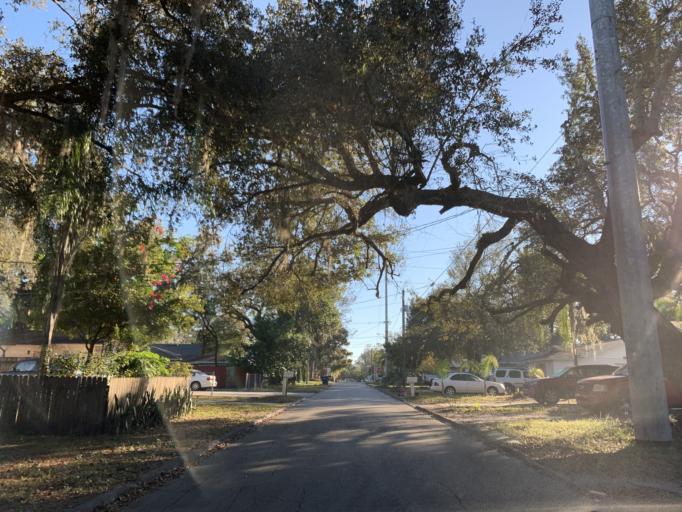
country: US
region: Florida
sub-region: Hillsborough County
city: University
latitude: 28.0392
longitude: -82.4317
